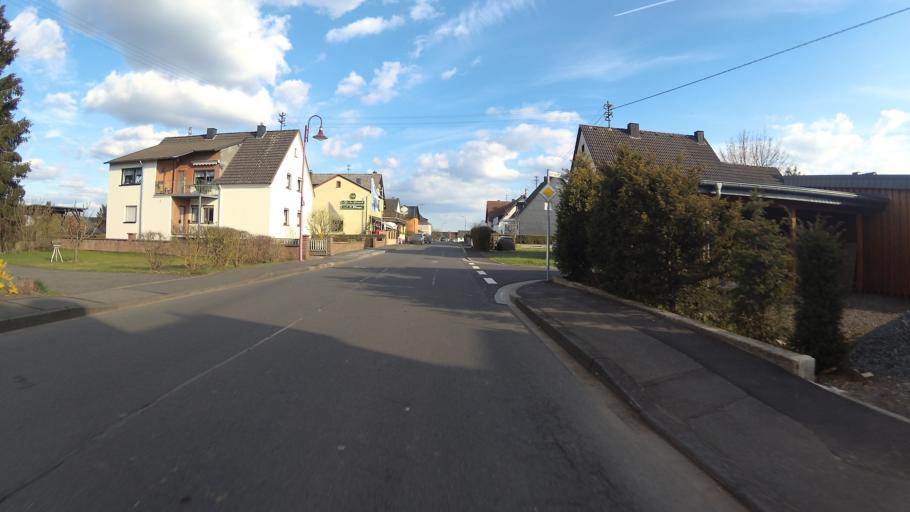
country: DE
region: Rheinland-Pfalz
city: Darscheid
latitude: 50.2145
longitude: 6.8891
